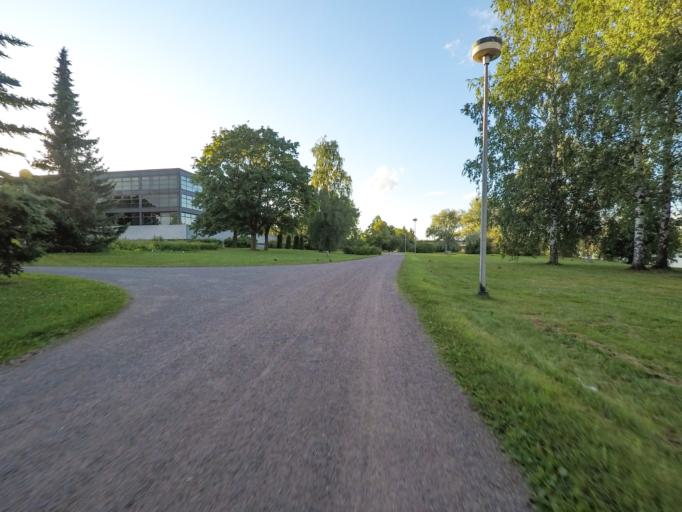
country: FI
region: South Karelia
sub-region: Imatra
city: Imatra
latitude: 61.1929
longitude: 28.7773
